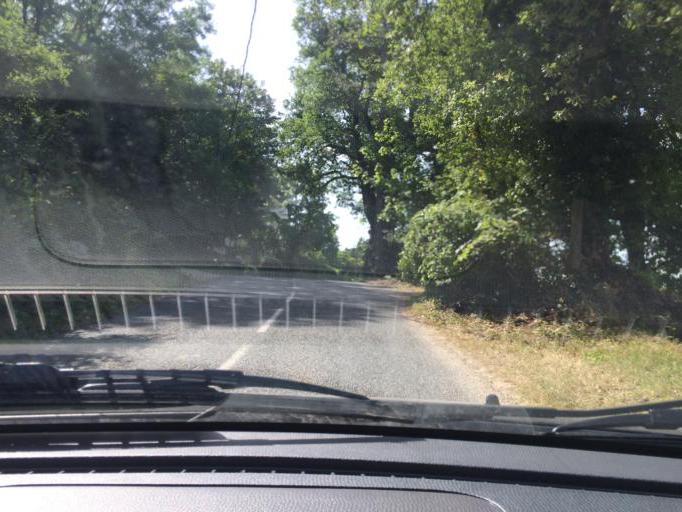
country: FR
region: Rhone-Alpes
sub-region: Departement du Rhone
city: Limonest
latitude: 45.8297
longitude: 4.7881
